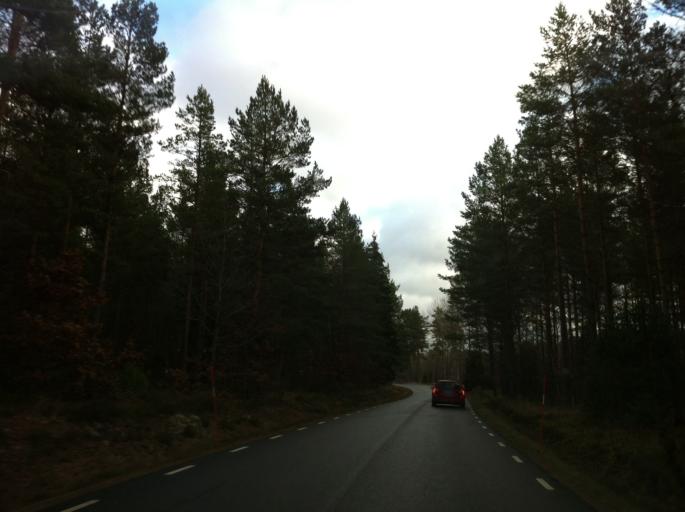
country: SE
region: Kalmar
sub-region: Hultsfreds Kommun
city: Hultsfred
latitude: 57.5302
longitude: 15.7624
